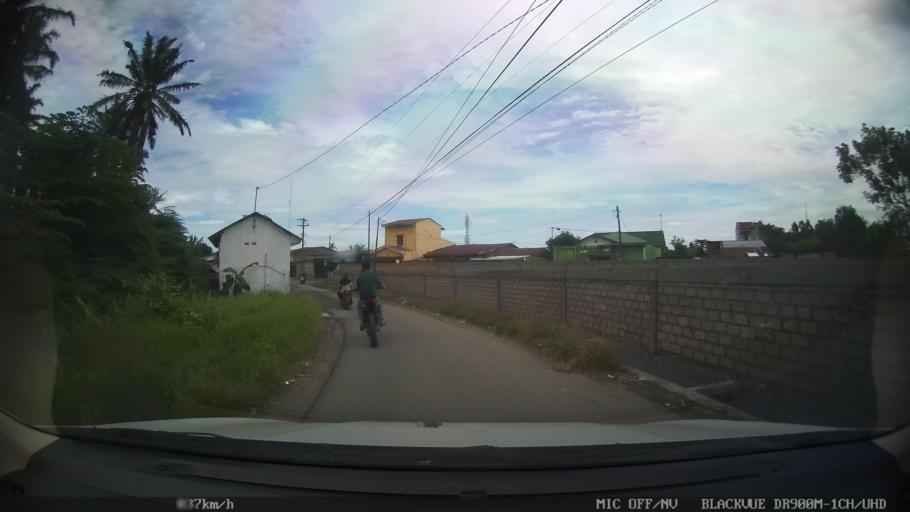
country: ID
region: North Sumatra
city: Sunggal
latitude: 3.5901
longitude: 98.5675
